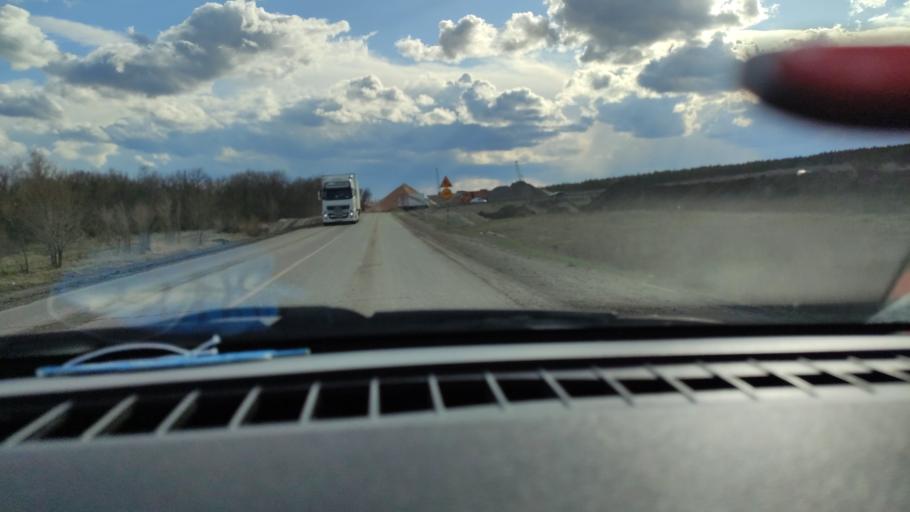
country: RU
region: Saratov
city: Sinodskoye
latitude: 52.0146
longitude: 46.6932
